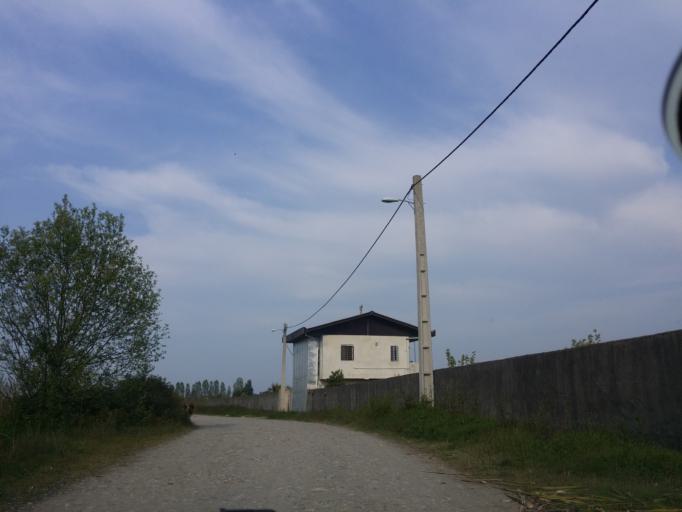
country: IR
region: Mazandaran
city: Chalus
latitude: 36.6804
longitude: 51.3939
